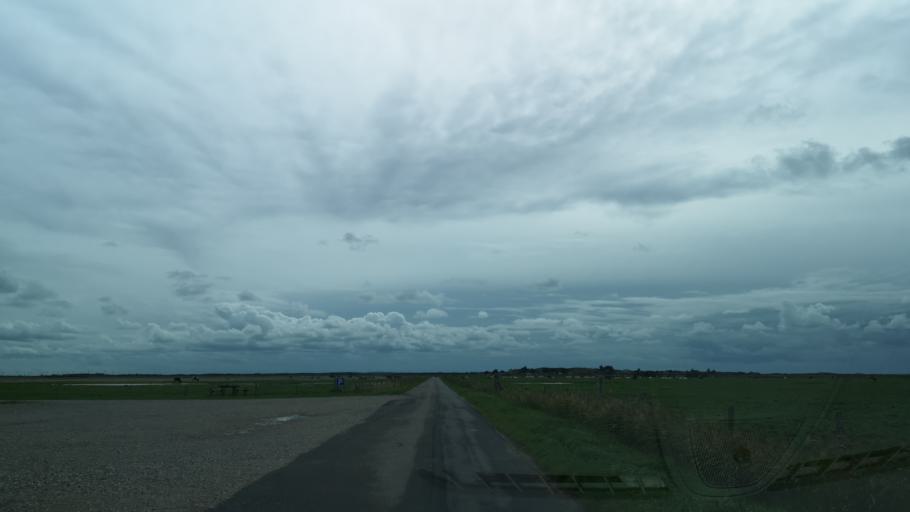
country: DK
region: Central Jutland
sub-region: Ringkobing-Skjern Kommune
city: Hvide Sande
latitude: 55.8620
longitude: 8.2202
